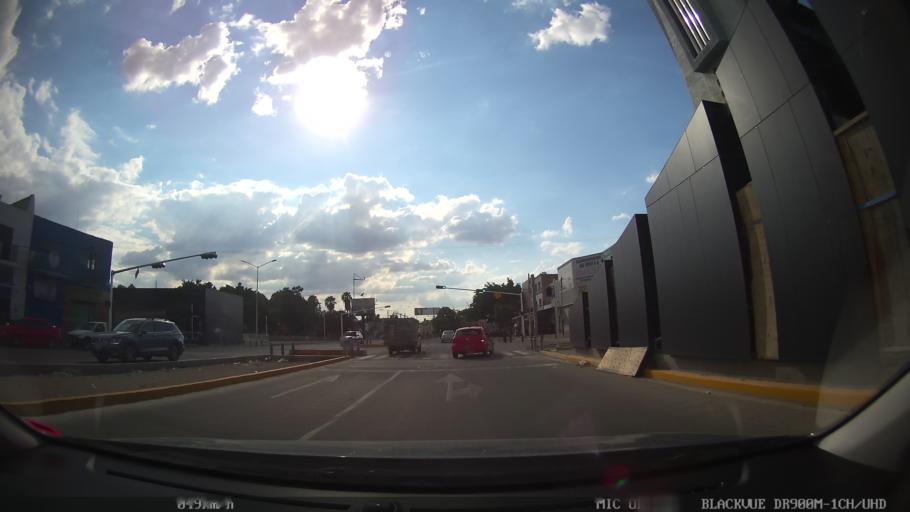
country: MX
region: Jalisco
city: Tlaquepaque
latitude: 20.6640
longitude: -103.3311
